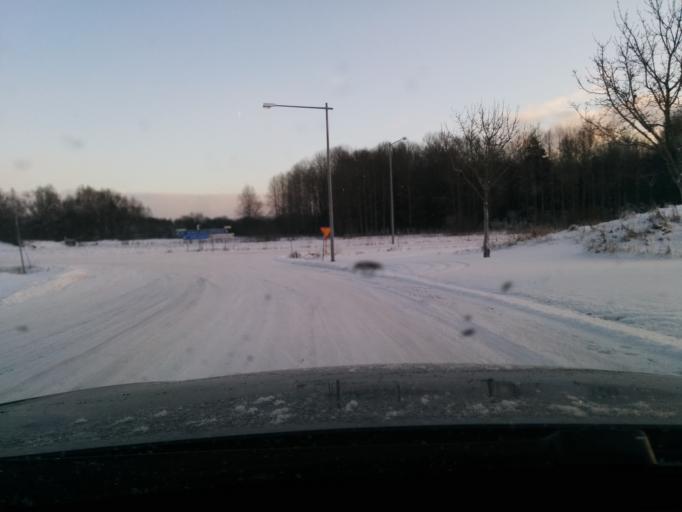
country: SE
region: Uppsala
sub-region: Tierps Kommun
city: Orbyhus
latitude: 60.2250
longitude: 17.7074
